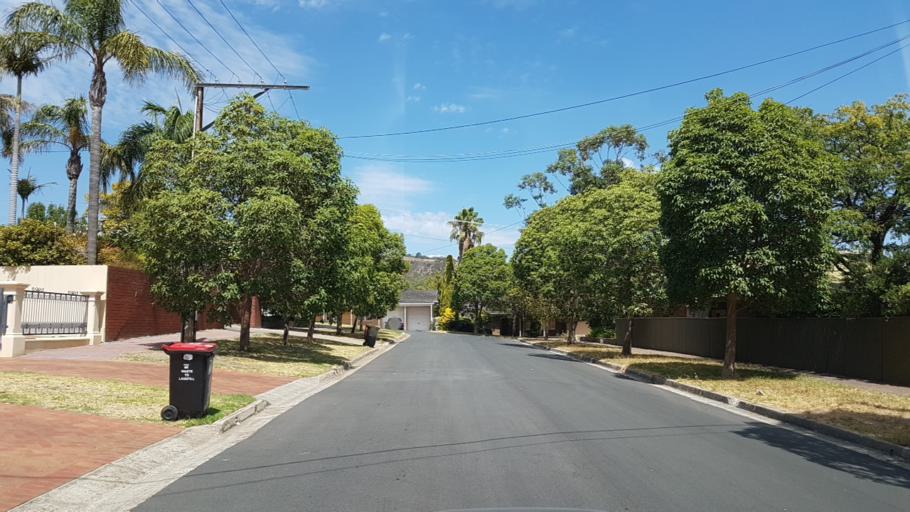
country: AU
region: South Australia
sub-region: Burnside
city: Hazelwood Park
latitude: -34.9394
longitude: 138.6645
